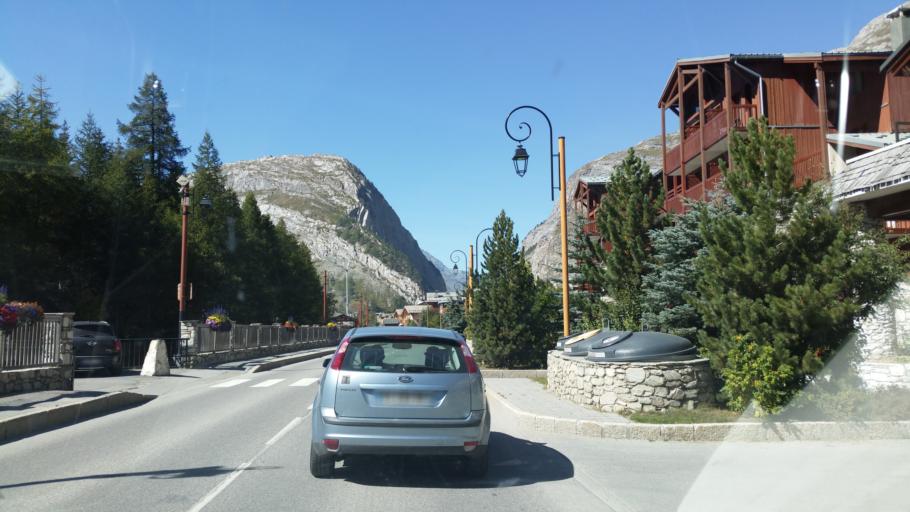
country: FR
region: Rhone-Alpes
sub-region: Departement de la Savoie
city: Val-d'Isere
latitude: 45.4518
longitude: 6.9745
